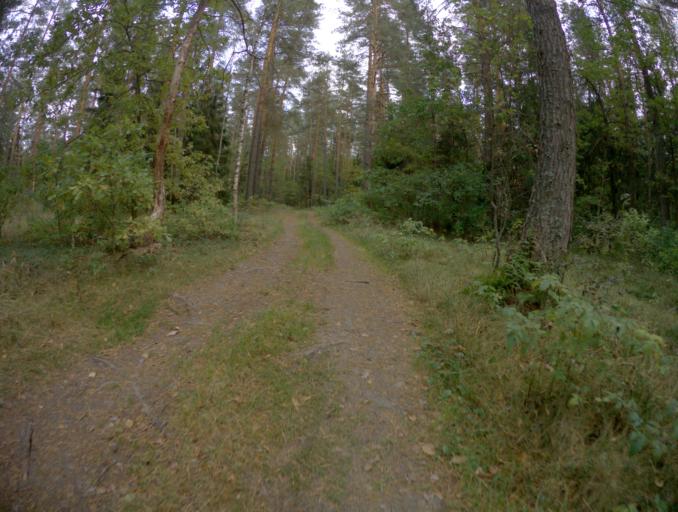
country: RU
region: Vladimir
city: Bogolyubovo
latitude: 56.1253
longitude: 40.5225
